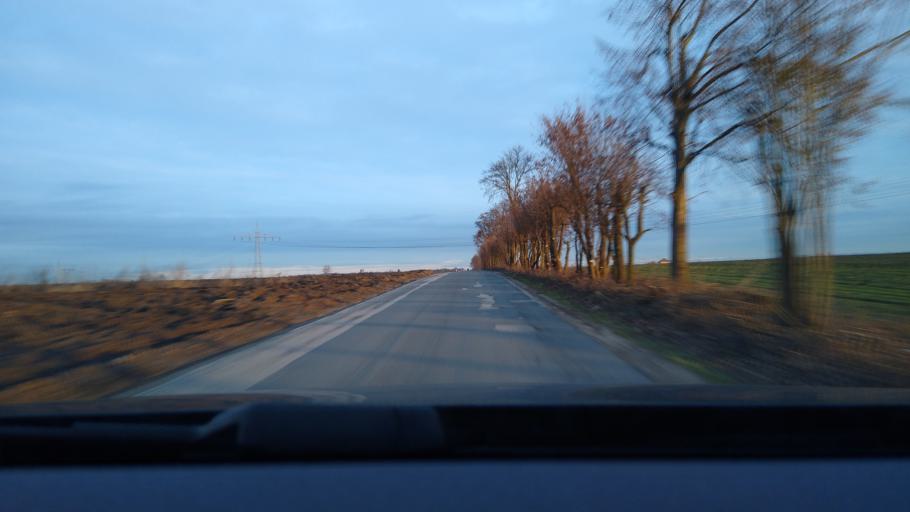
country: DE
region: Bavaria
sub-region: Regierungsbezirk Mittelfranken
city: Wetzendorf
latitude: 49.4882
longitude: 11.0203
